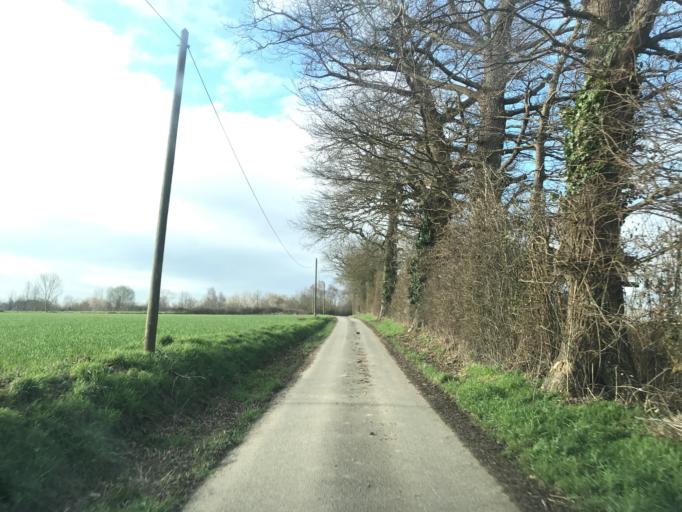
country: FR
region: Lower Normandy
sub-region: Departement du Calvados
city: Dives-sur-Mer
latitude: 49.2247
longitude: -0.1059
